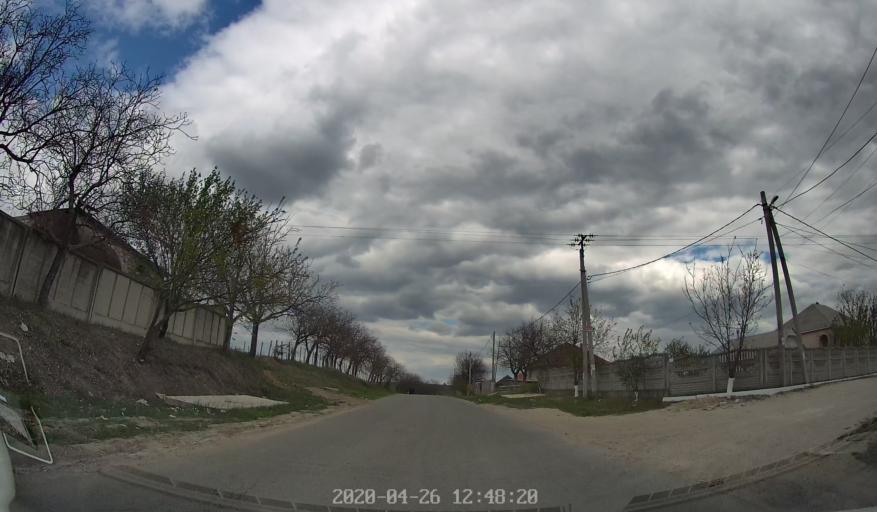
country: MD
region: Chisinau
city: Vadul lui Voda
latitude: 47.0682
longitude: 29.0154
